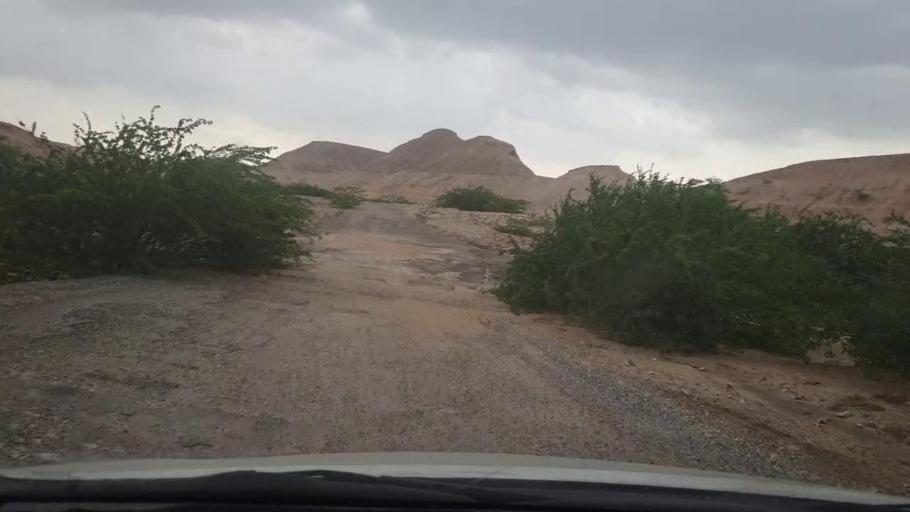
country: PK
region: Sindh
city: Khairpur
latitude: 27.4708
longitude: 68.9143
